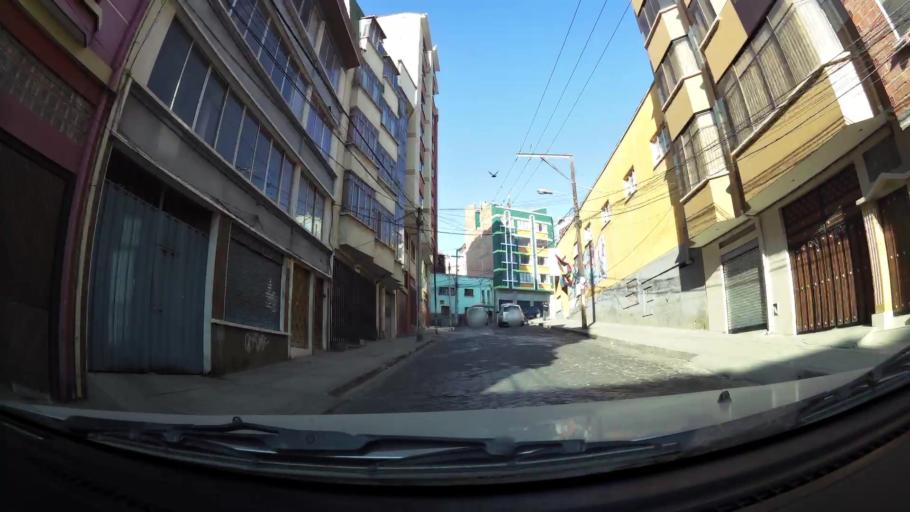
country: BO
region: La Paz
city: La Paz
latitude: -16.5042
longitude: -68.1389
